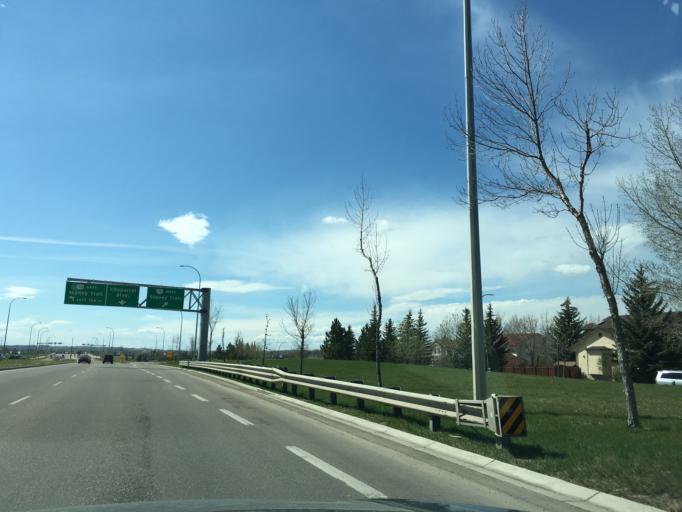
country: CA
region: Alberta
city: Calgary
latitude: 50.8977
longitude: -114.0248
